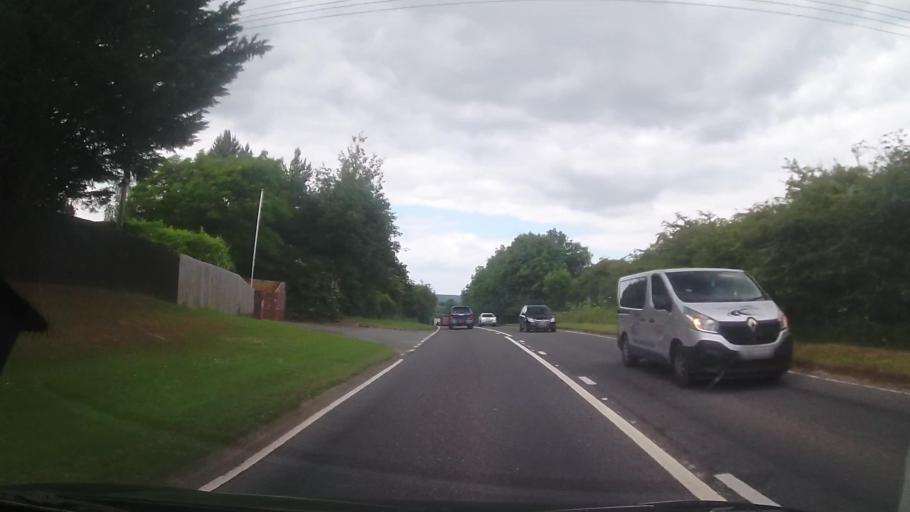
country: GB
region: England
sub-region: Herefordshire
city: Wellington
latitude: 52.0961
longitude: -2.7294
